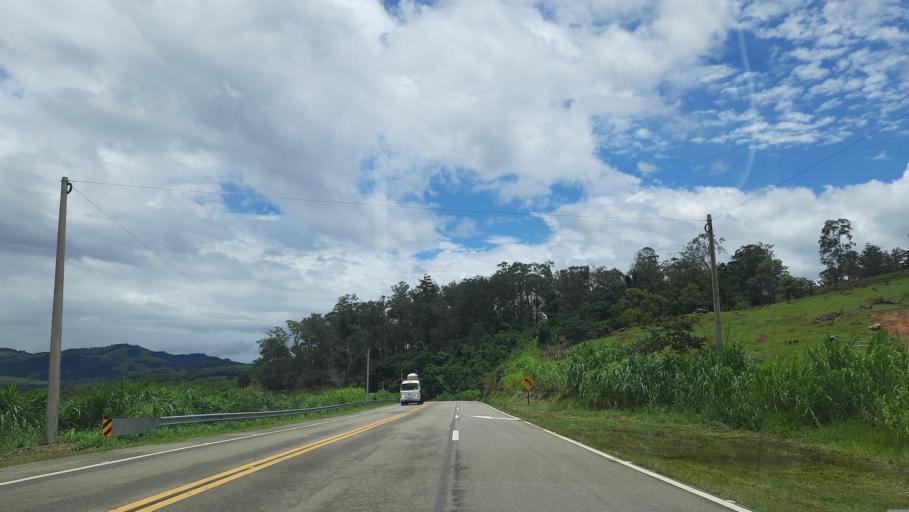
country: BR
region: Sao Paulo
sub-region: Vargem Grande Do Sul
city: Vargem Grande do Sul
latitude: -21.7993
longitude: -46.8173
